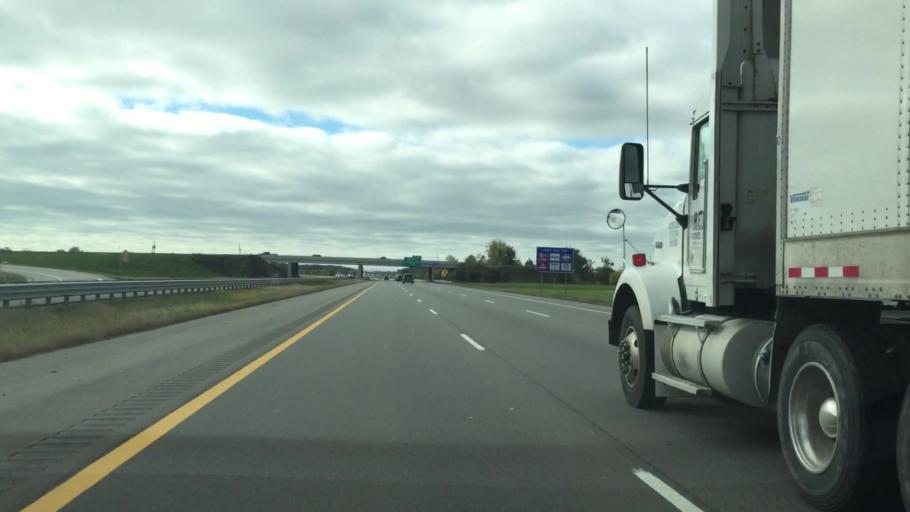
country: US
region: Michigan
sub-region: Macomb County
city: Mount Clemens
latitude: 42.6479
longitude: -82.8391
